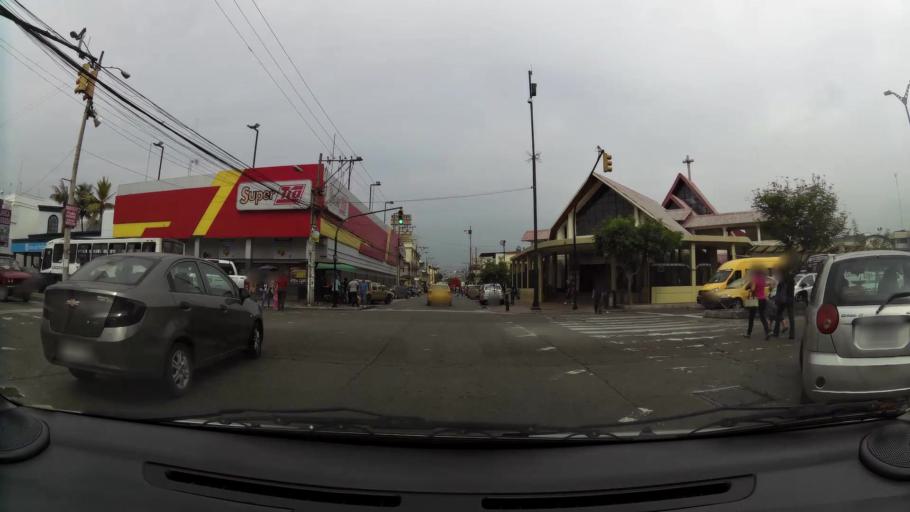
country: EC
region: Guayas
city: Eloy Alfaro
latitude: -2.1394
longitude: -79.8984
